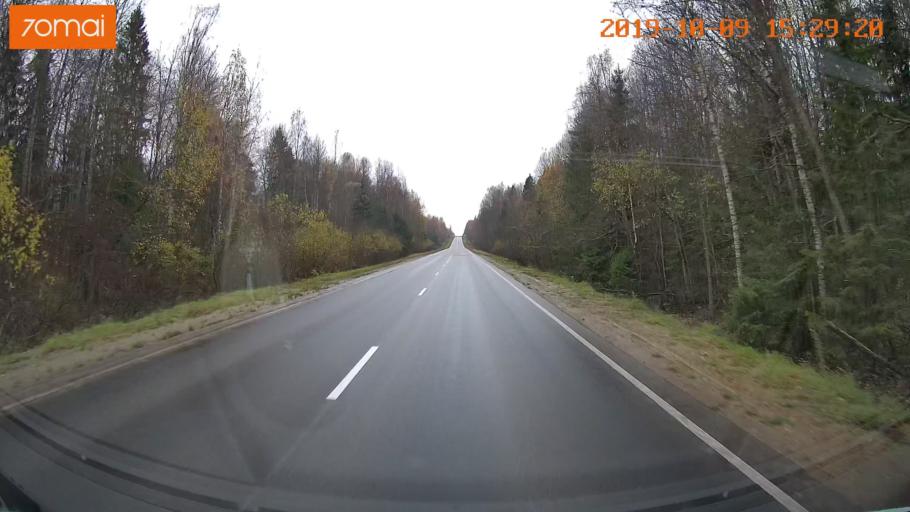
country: RU
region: Kostroma
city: Susanino
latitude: 57.9927
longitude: 41.3446
